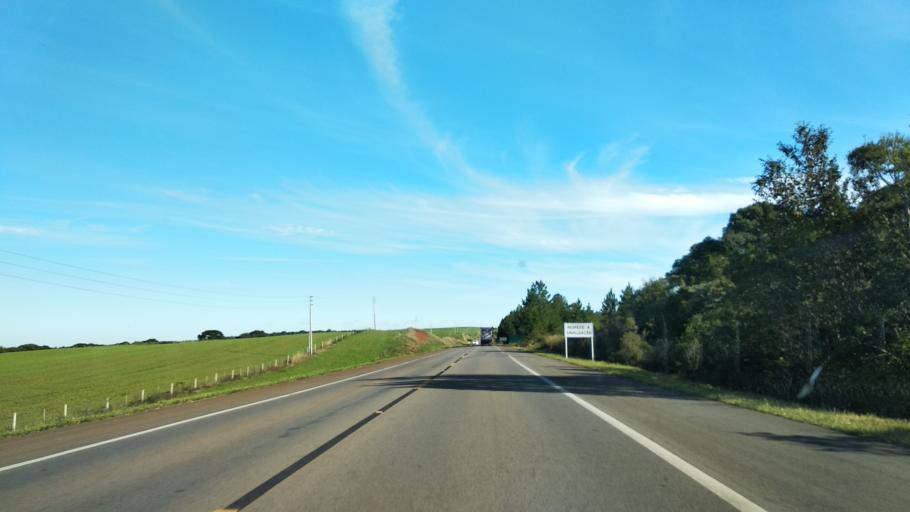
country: BR
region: Santa Catarina
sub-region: Celso Ramos
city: Celso Ramos
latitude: -27.5087
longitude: -51.3461
